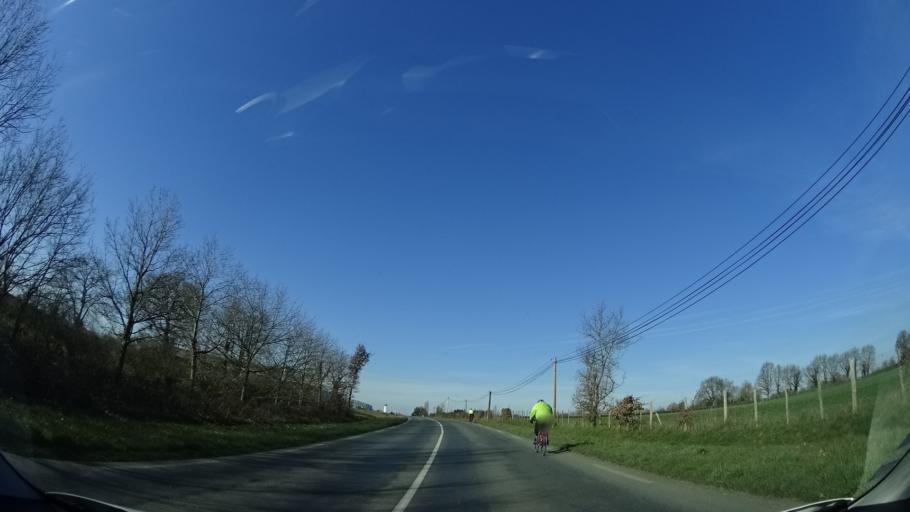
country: FR
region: Poitou-Charentes
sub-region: Departement des Deux-Sevres
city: Chiche
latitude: 46.8333
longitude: -0.3711
